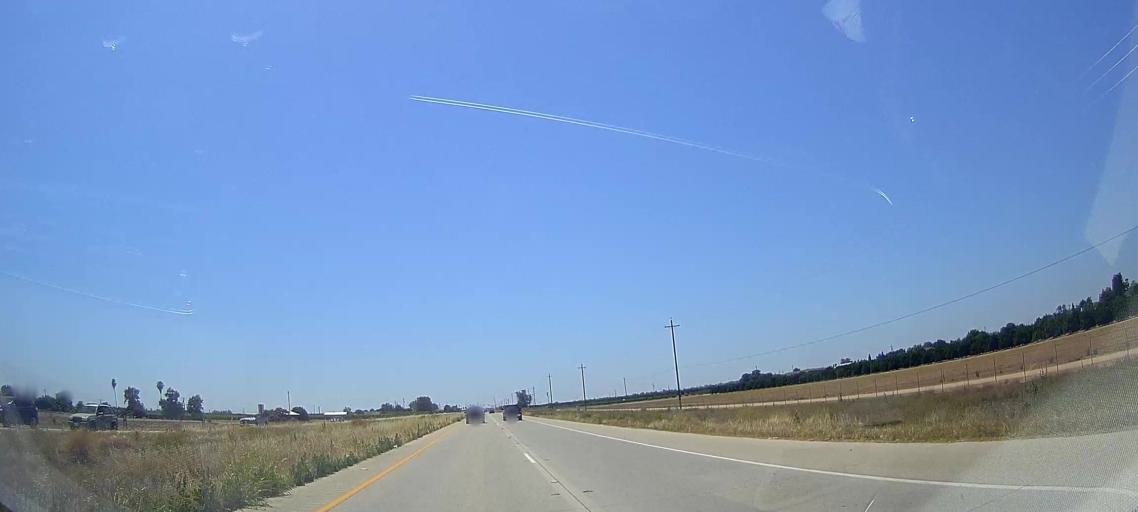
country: US
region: California
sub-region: Fresno County
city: Sanger
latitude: 36.7361
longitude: -119.5669
